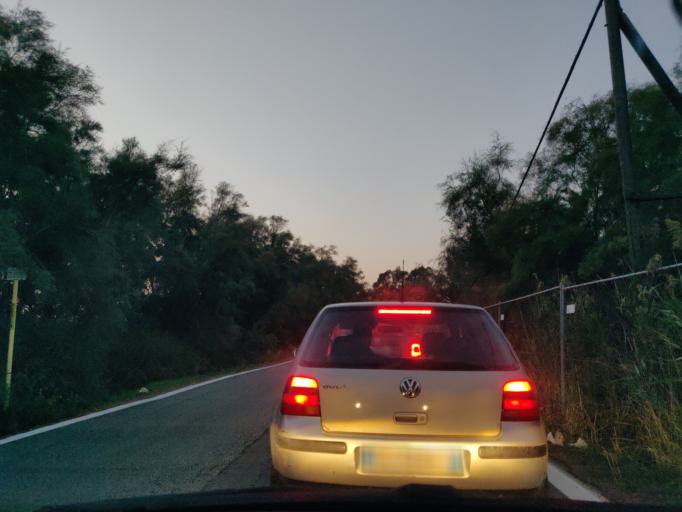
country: IT
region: Latium
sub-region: Citta metropolitana di Roma Capitale
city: Npp 23 (Parco Leonardo)
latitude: 41.8255
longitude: 12.2894
